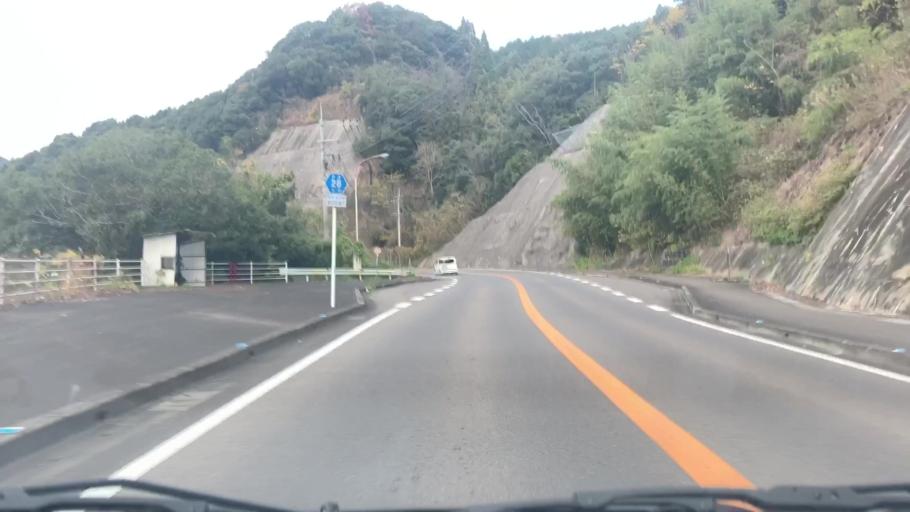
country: JP
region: Saga Prefecture
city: Ureshinomachi-shimojuku
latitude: 33.1363
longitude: 130.0248
